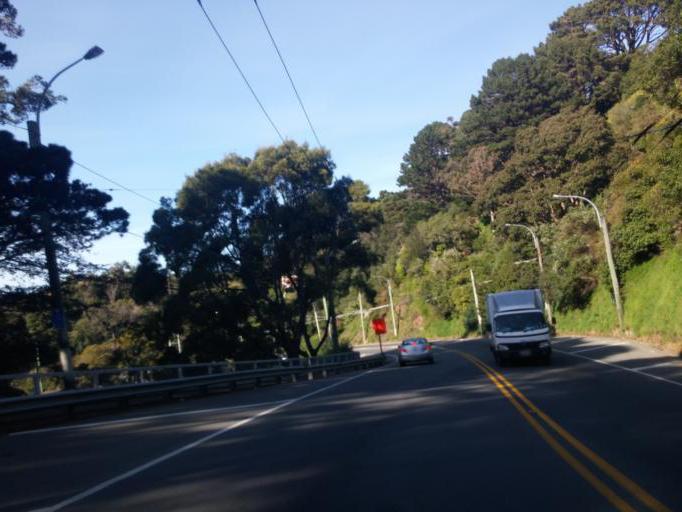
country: NZ
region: Wellington
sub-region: Wellington City
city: Wellington
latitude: -41.3026
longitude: 174.7680
